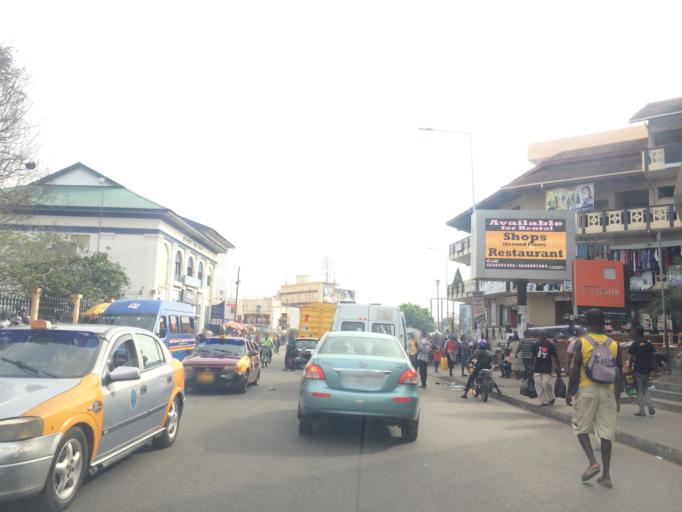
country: GH
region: Greater Accra
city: Accra
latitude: 5.5467
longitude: -0.2059
